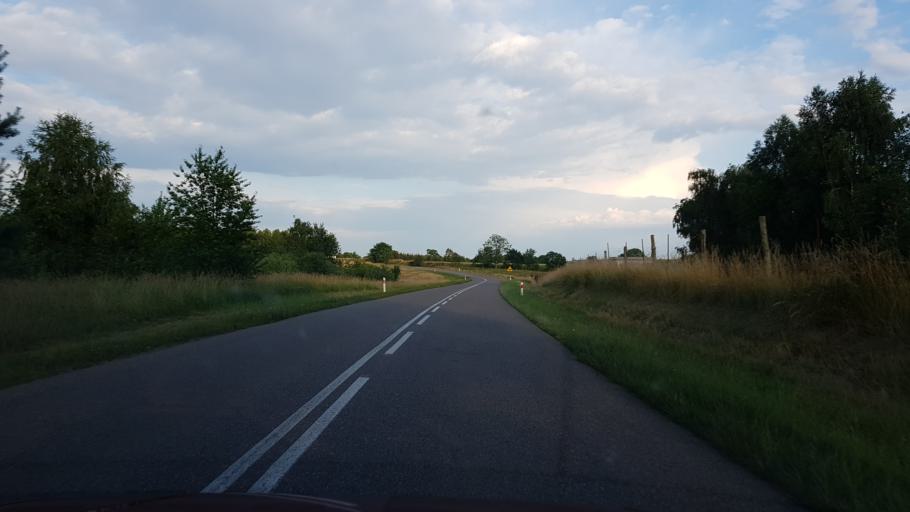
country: PL
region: West Pomeranian Voivodeship
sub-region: Powiat goleniowski
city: Nowogard
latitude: 53.6921
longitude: 15.0696
